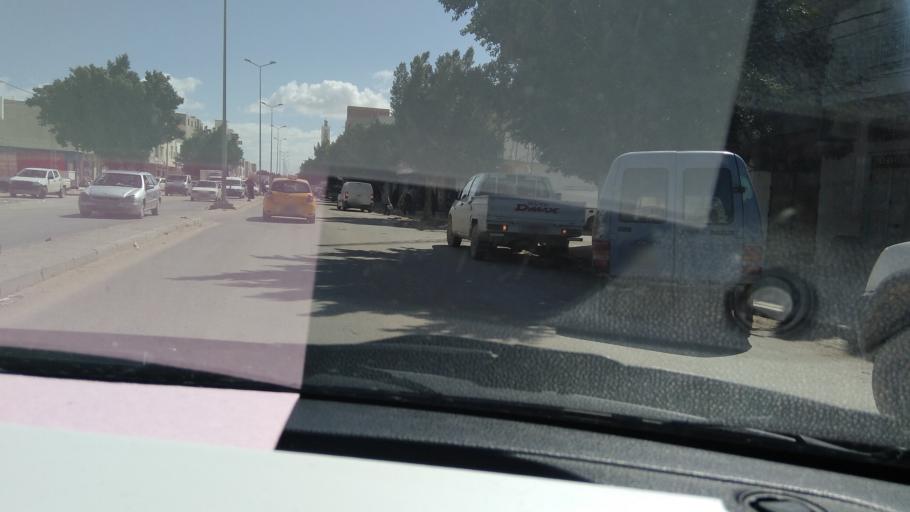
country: TN
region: Al Qayrawan
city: Kairouan
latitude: 35.6822
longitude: 10.0795
